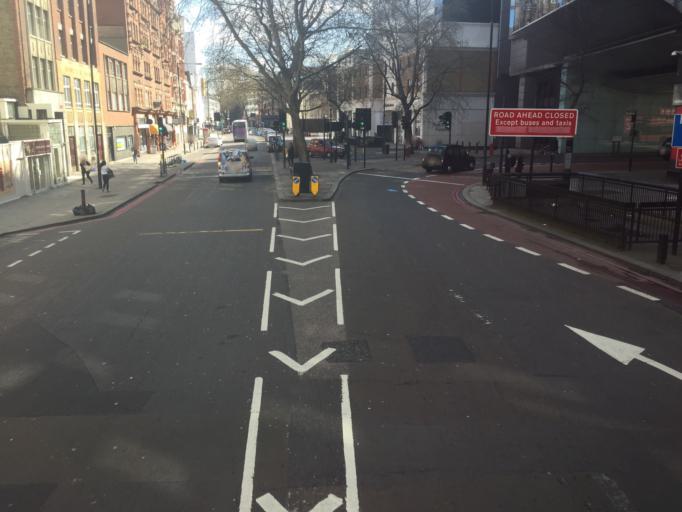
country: GB
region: England
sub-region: Greater London
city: London
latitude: 51.4953
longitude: -0.1418
